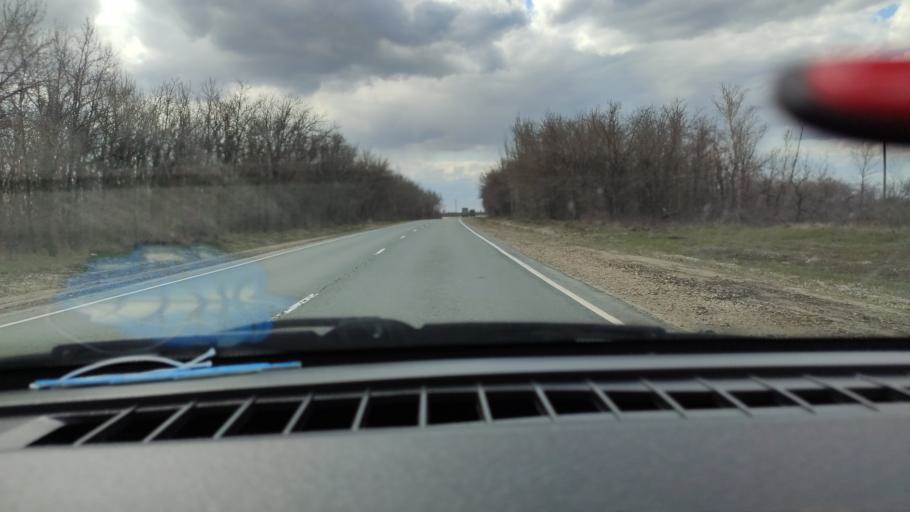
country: RU
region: Saratov
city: Alekseyevka
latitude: 52.2685
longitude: 47.9271
